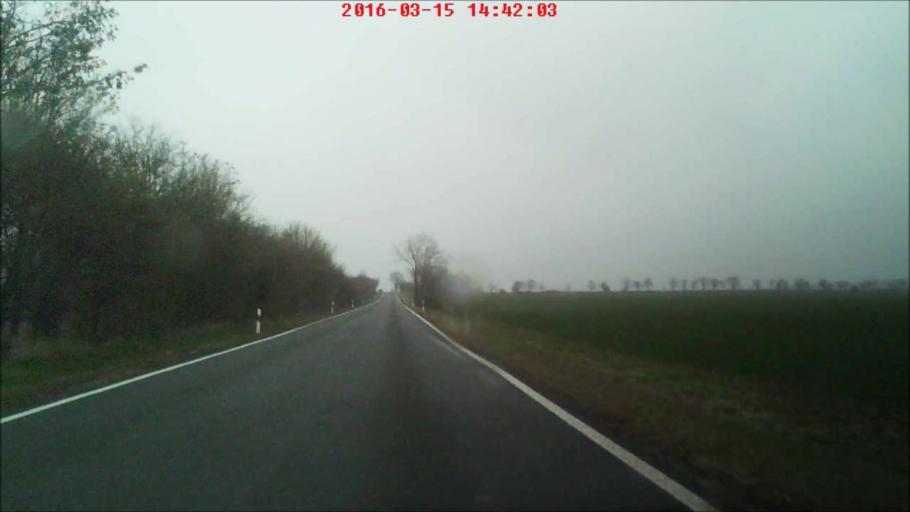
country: DE
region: Thuringia
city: Elxleben
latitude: 50.8773
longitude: 11.0545
